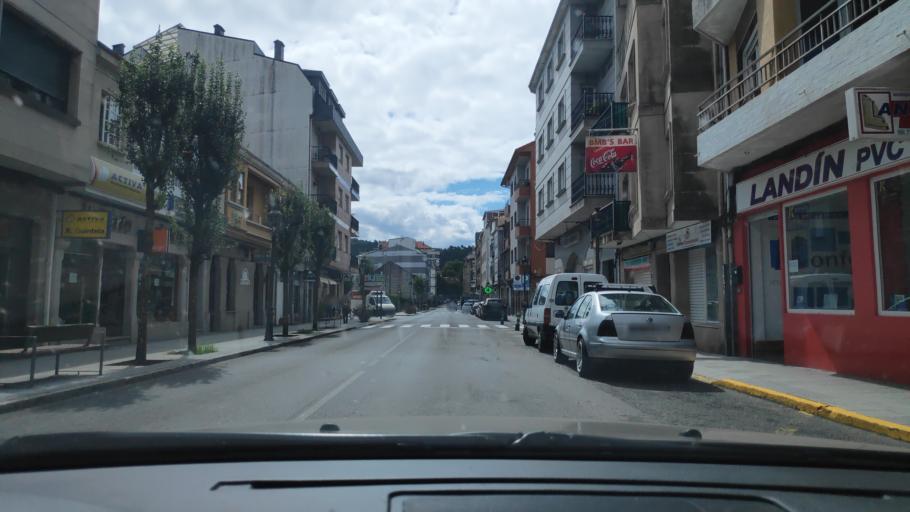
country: ES
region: Galicia
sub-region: Provincia de Pontevedra
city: Caldas de Reis
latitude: 42.6066
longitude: -8.6444
